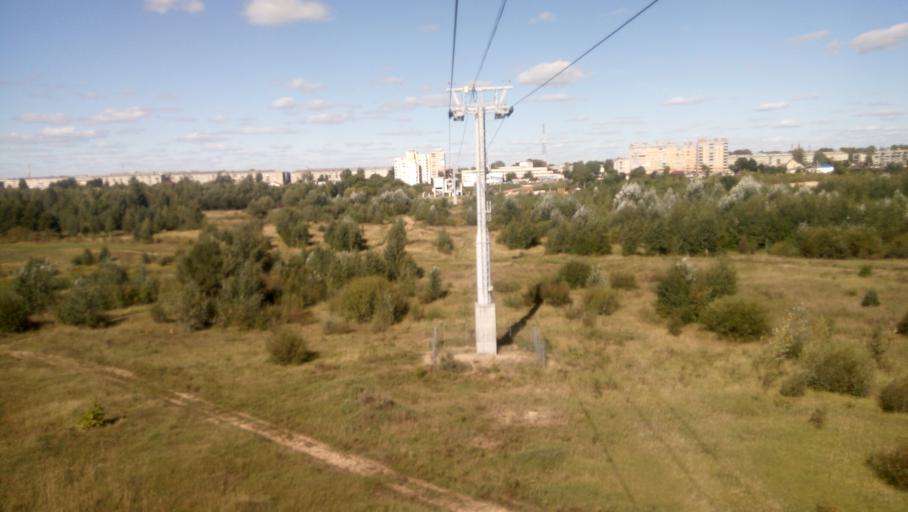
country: RU
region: Nizjnij Novgorod
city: Bor
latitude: 56.3492
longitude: 44.0576
